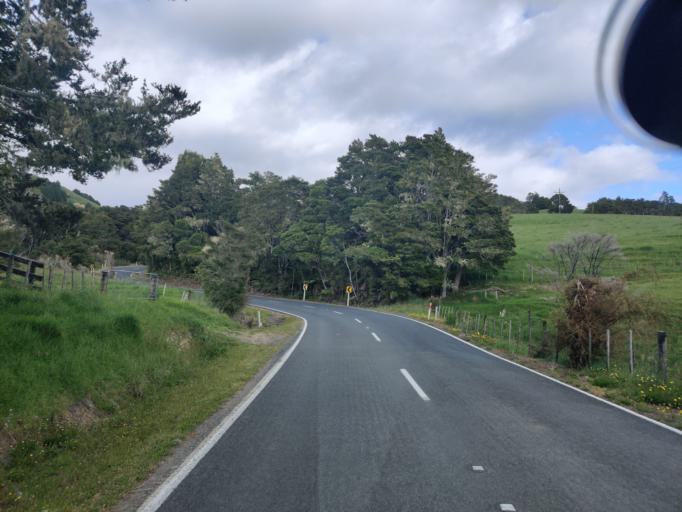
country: NZ
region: Northland
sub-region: Whangarei
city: Ngunguru
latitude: -35.5785
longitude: 174.4170
